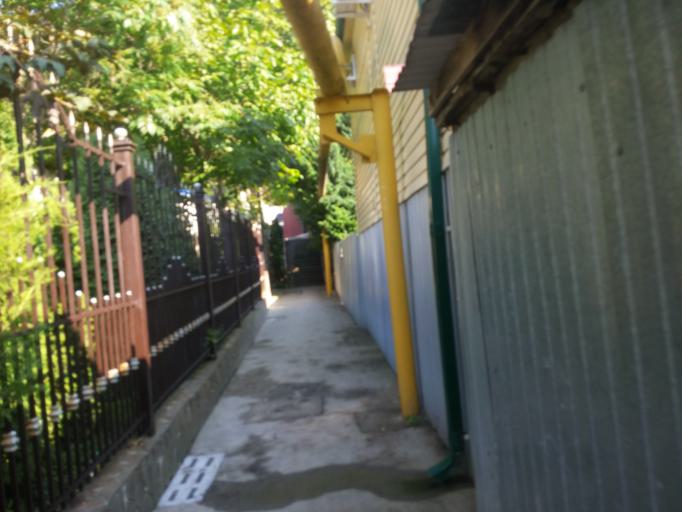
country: RU
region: Krasnodarskiy
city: Divnomorskoye
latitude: 44.4647
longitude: 38.1574
